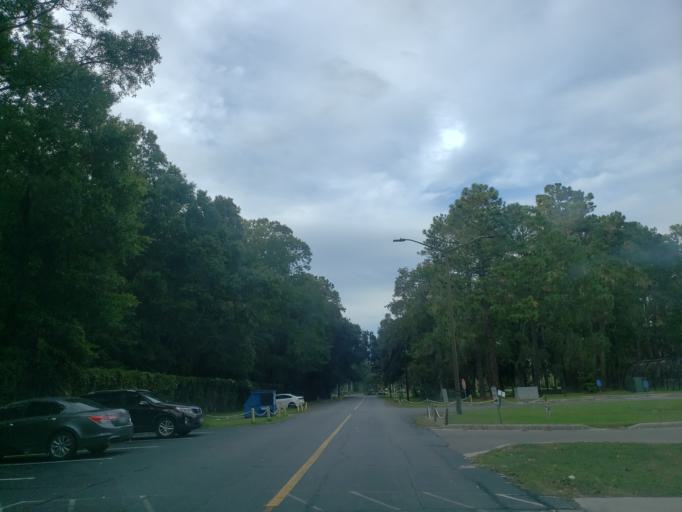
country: US
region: Georgia
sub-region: Chatham County
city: Isle of Hope
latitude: 31.9999
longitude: -81.0840
